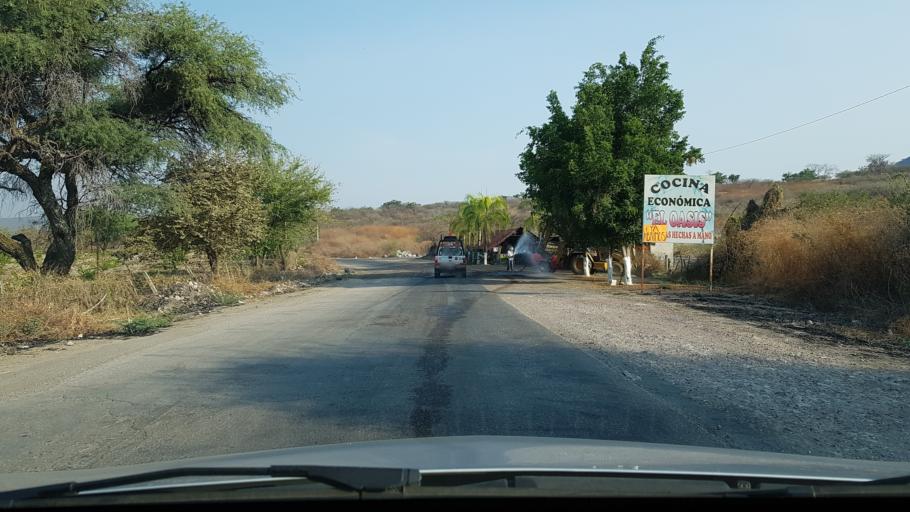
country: MX
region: Morelos
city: Tlaltizapan
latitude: 18.6841
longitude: -99.0891
